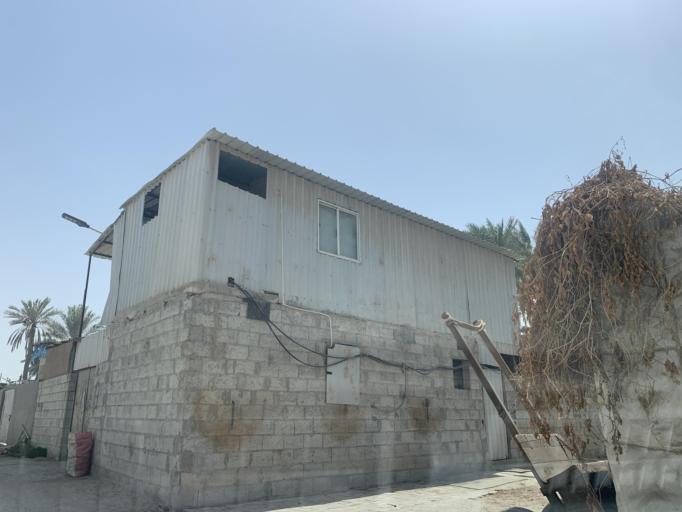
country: BH
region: Central Governorate
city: Madinat Hamad
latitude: 26.1498
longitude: 50.4953
